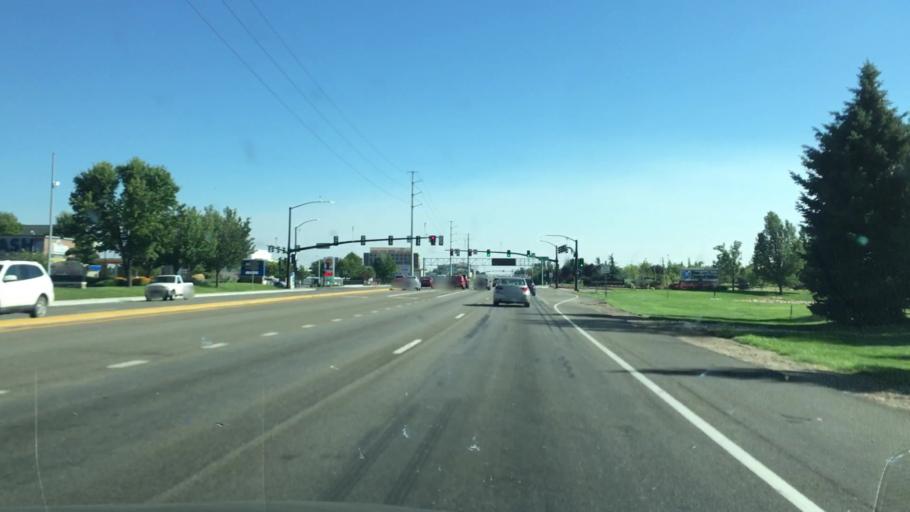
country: US
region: Idaho
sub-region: Ada County
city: Meridian
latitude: 43.6135
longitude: -116.3548
